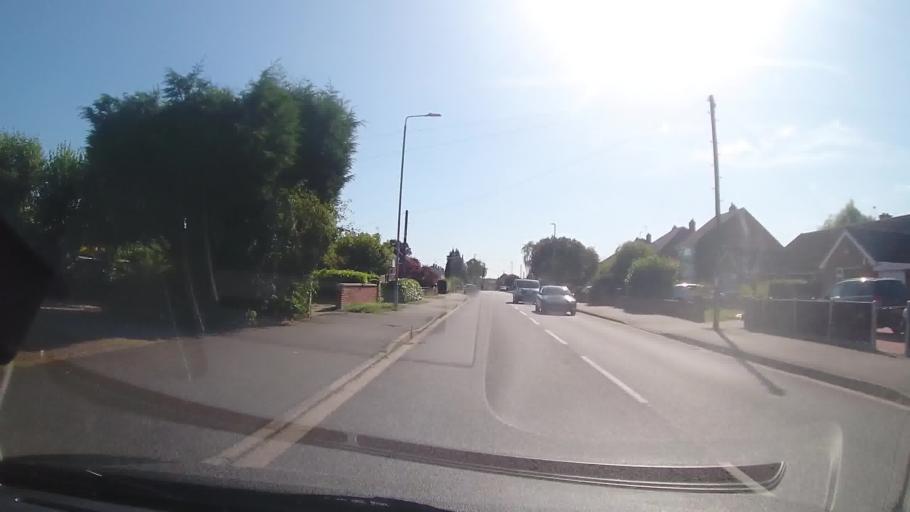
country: GB
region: England
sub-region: Leicestershire
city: Glenfield
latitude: 52.6414
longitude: -1.1920
